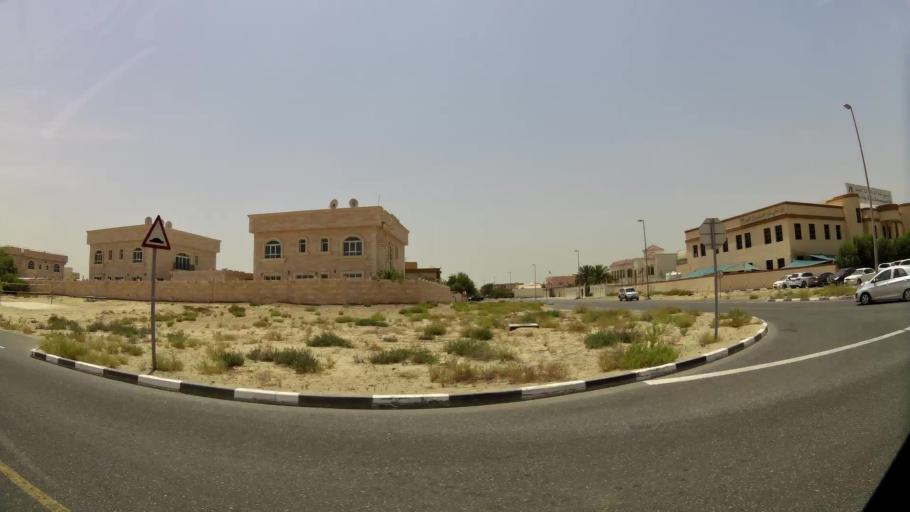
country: AE
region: Ash Shariqah
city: Sharjah
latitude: 25.1930
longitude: 55.3891
